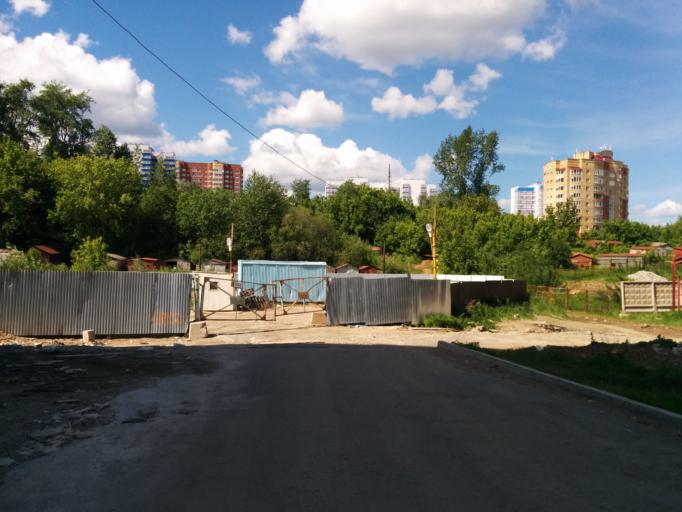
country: RU
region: Perm
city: Perm
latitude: 58.0113
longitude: 56.3030
